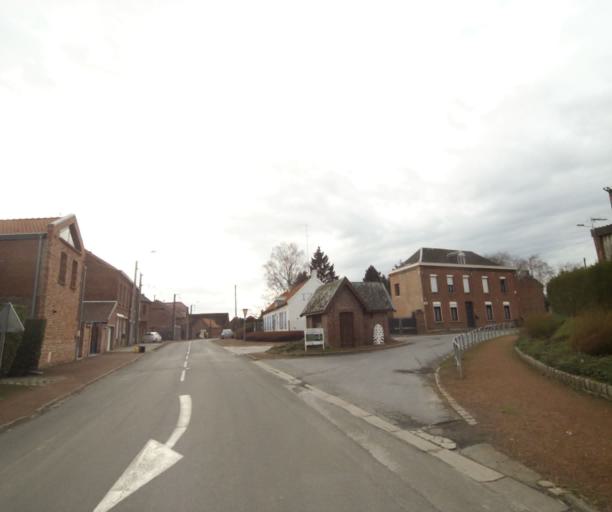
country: FR
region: Nord-Pas-de-Calais
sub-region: Departement du Nord
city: Sebourg
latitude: 50.3649
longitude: 3.6470
